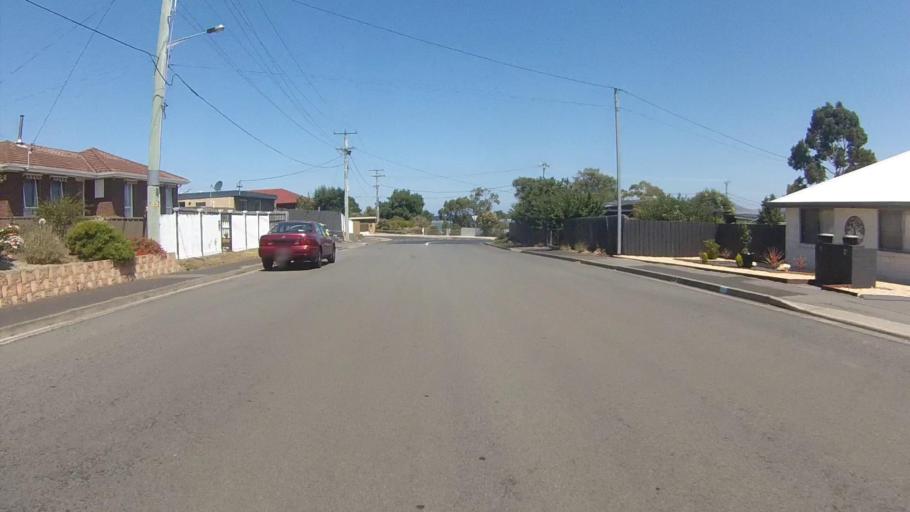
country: AU
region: Tasmania
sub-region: Sorell
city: Sorell
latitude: -42.8021
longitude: 147.5346
